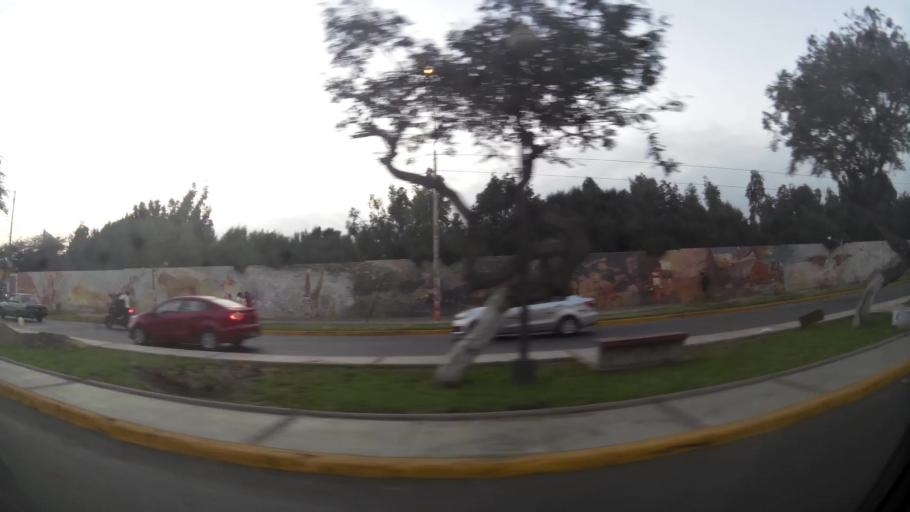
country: PE
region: La Libertad
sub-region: Provincia de Trujillo
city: Trujillo
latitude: -8.1189
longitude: -79.0399
